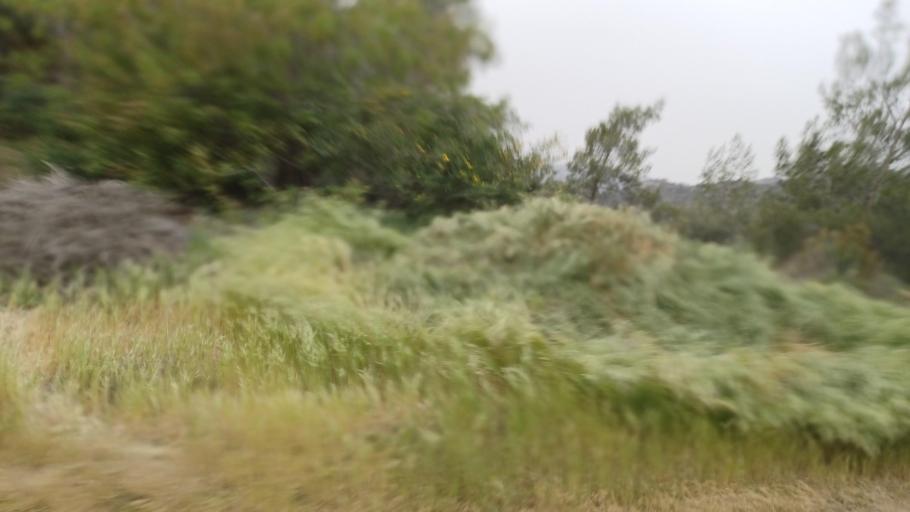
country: CY
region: Limassol
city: Parekklisha
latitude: 34.8604
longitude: 33.0949
